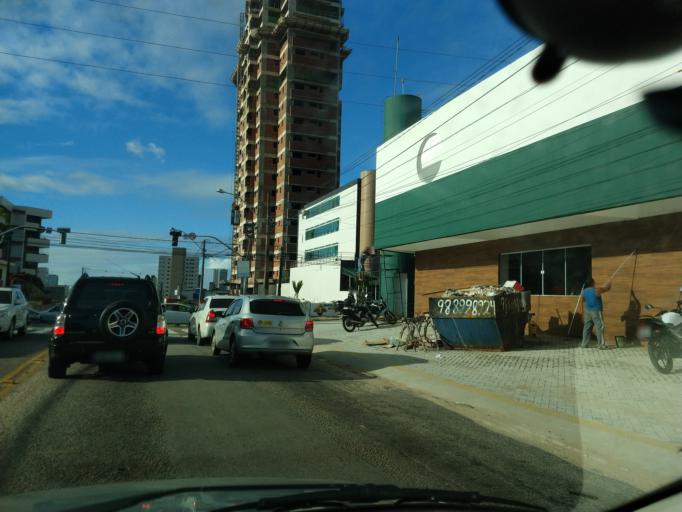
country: BR
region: Rio Grande do Norte
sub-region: Natal
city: Natal
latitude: -5.8300
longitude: -35.2223
